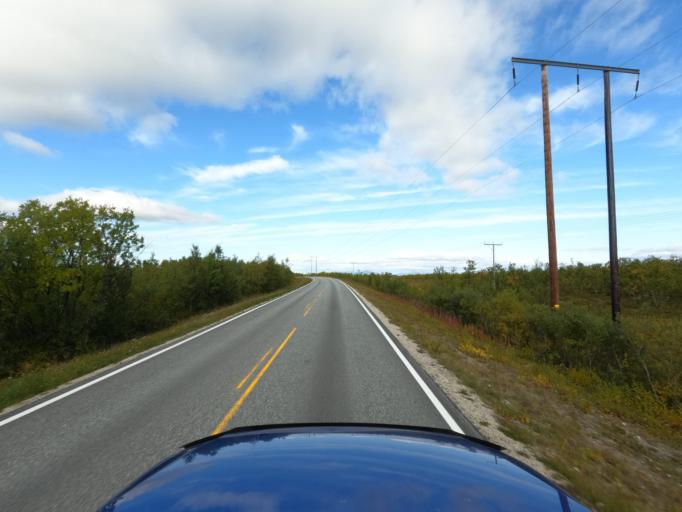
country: NO
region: Finnmark Fylke
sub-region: Karasjok
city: Karasjohka
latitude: 69.6633
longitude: 25.2762
